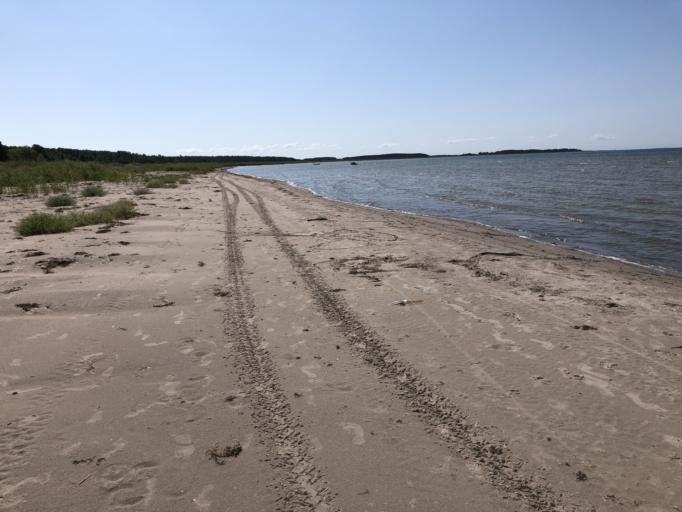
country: EE
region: Hiiumaa
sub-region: Kaerdla linn
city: Kardla
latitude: 58.7754
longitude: 22.4777
